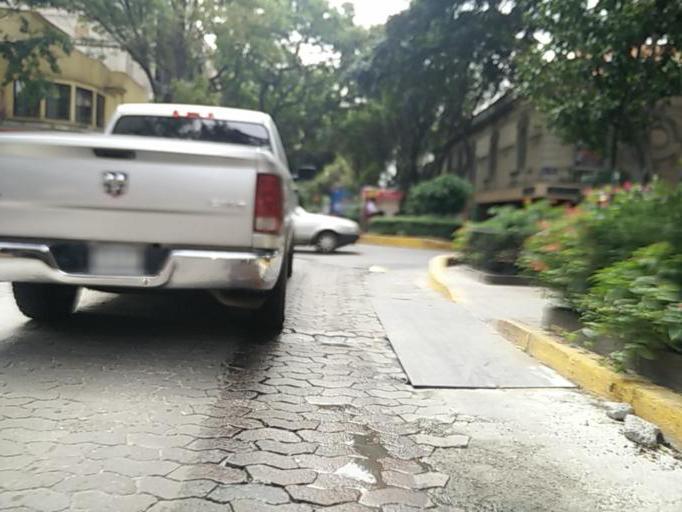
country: MX
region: Mexico City
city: Cuauhtemoc
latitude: 19.4262
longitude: -99.1655
